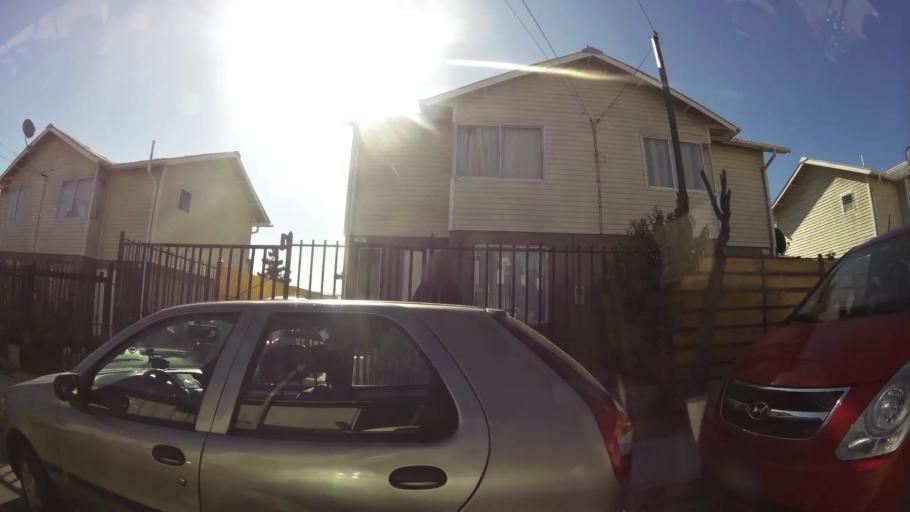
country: CL
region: Valparaiso
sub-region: Provincia de Valparaiso
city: Valparaiso
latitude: -33.1185
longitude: -71.5848
